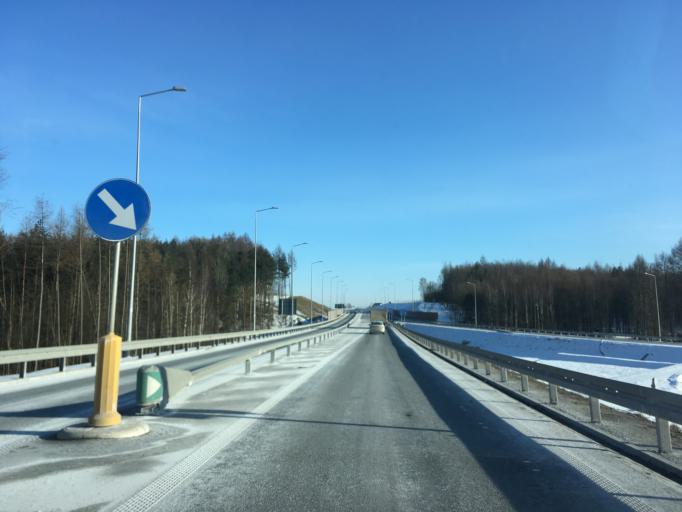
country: PL
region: Pomeranian Voivodeship
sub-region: Powiat koscierski
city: Koscierzyna
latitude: 54.1110
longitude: 17.9546
